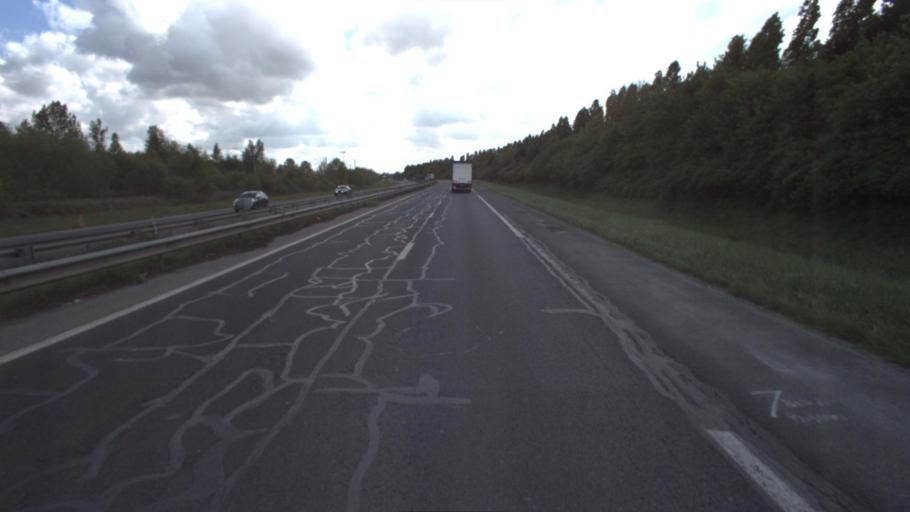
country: FR
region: Ile-de-France
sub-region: Departement de Seine-et-Marne
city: Tournan-en-Brie
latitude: 48.7297
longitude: 2.7997
